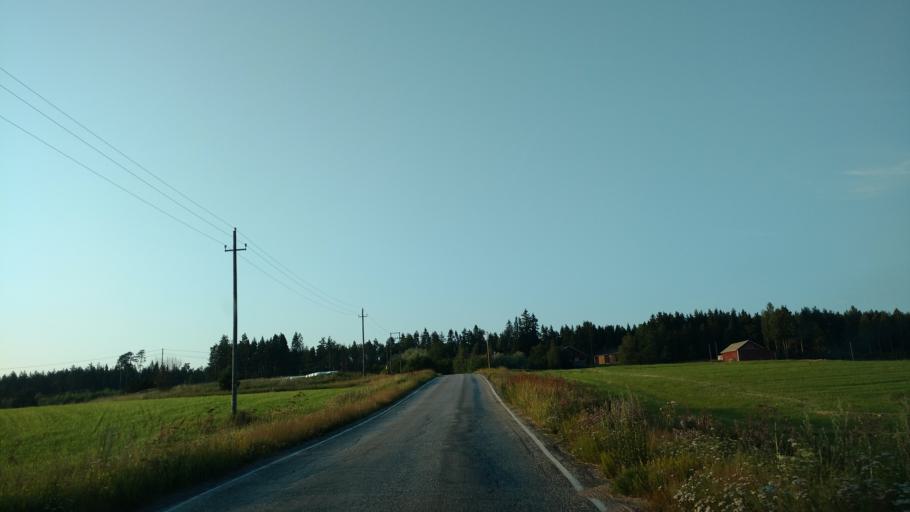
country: FI
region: Varsinais-Suomi
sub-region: Salo
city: Saerkisalo
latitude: 60.1771
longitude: 22.9658
